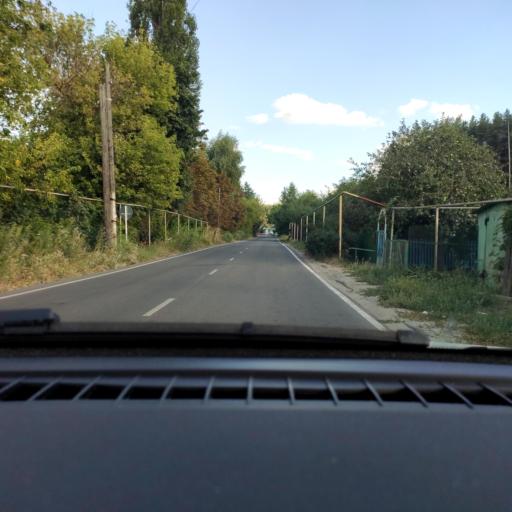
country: RU
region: Voronezj
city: Devitsa
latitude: 51.6569
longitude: 38.9767
